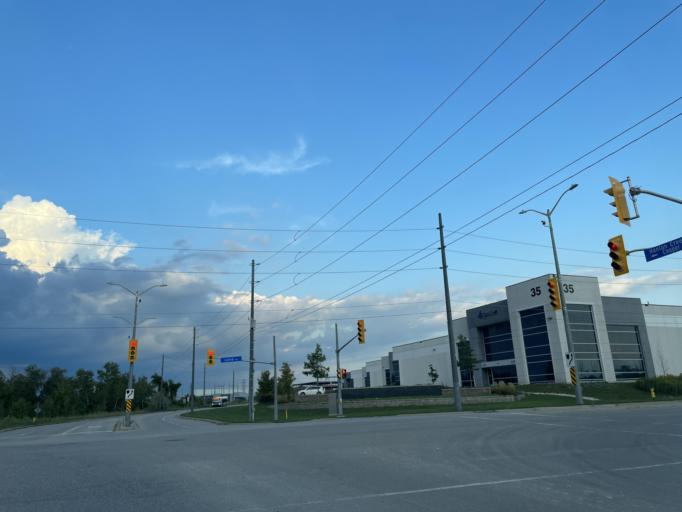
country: CA
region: Ontario
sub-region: Wellington County
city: Guelph
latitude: 43.4856
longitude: -80.2150
